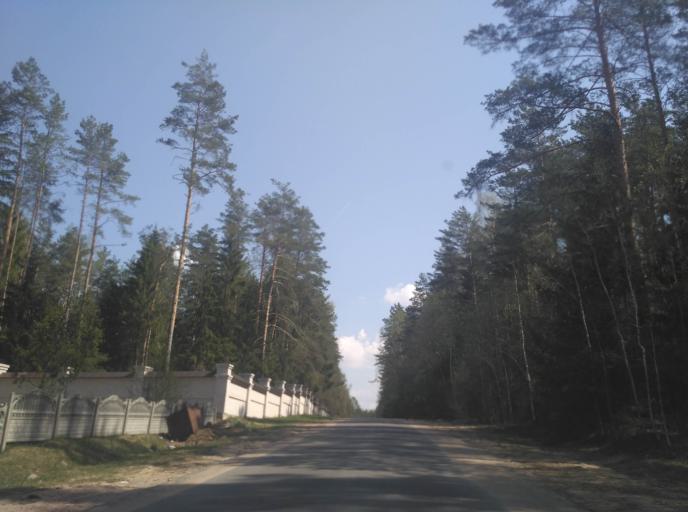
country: BY
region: Minsk
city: Loshnitsa
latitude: 54.4932
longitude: 28.6825
